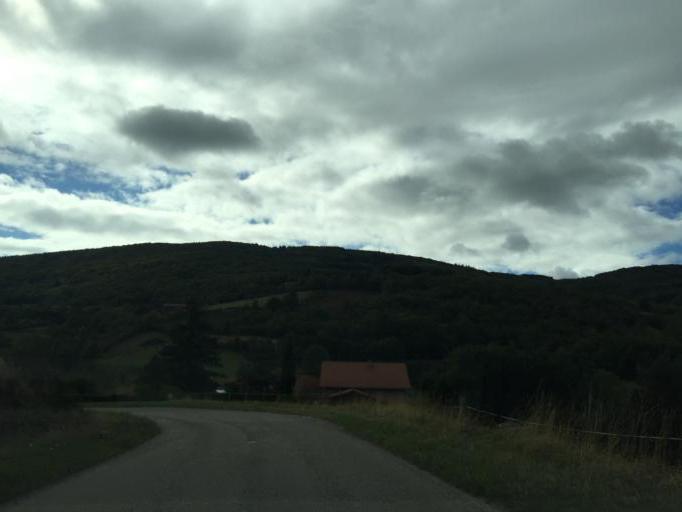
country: FR
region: Rhone-Alpes
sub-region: Departement de la Loire
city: Chateauneuf
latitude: 45.4706
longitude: 4.6591
